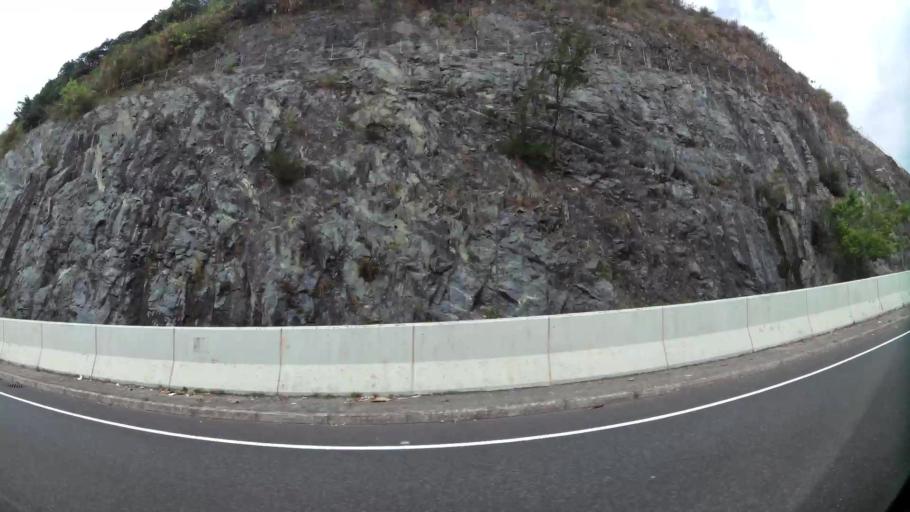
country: HK
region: Wanchai
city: Wan Chai
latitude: 22.2736
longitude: 114.2393
